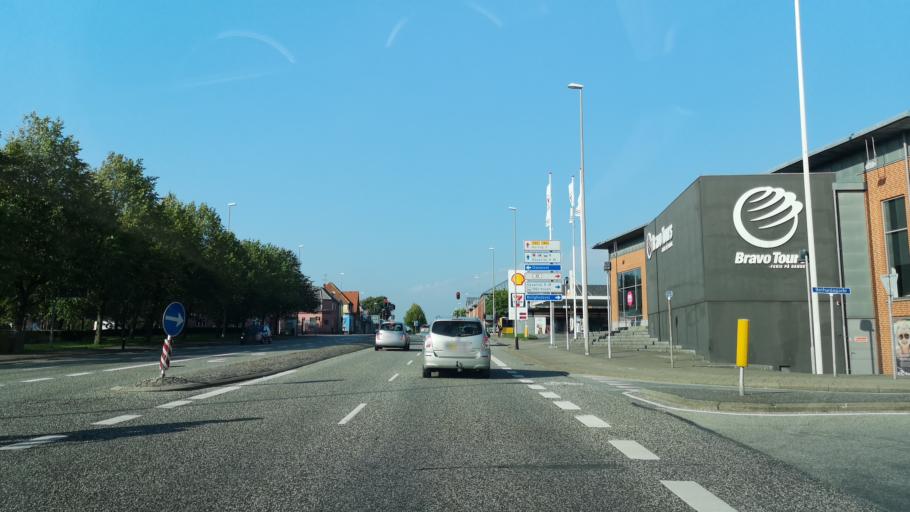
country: DK
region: Central Jutland
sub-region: Herning Kommune
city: Herning
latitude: 56.1372
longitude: 8.9673
